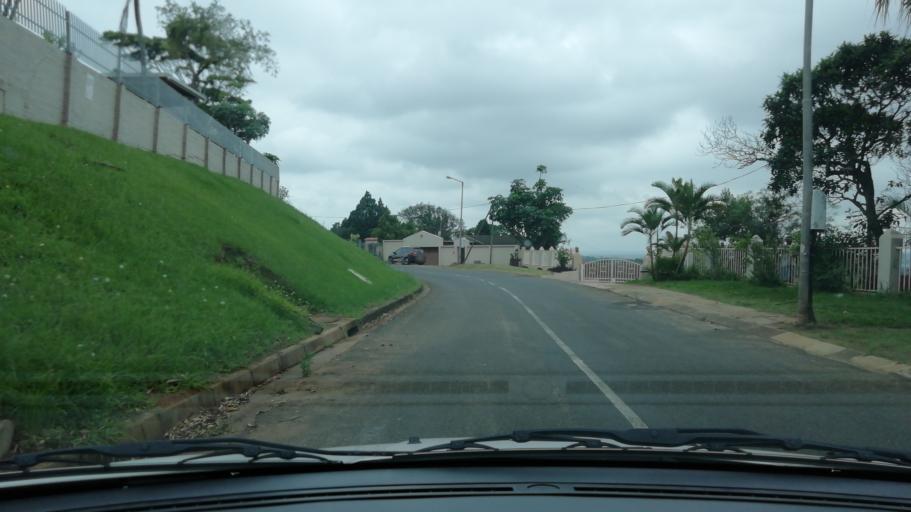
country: ZA
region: KwaZulu-Natal
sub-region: uThungulu District Municipality
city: Empangeni
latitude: -28.7476
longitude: 31.8951
